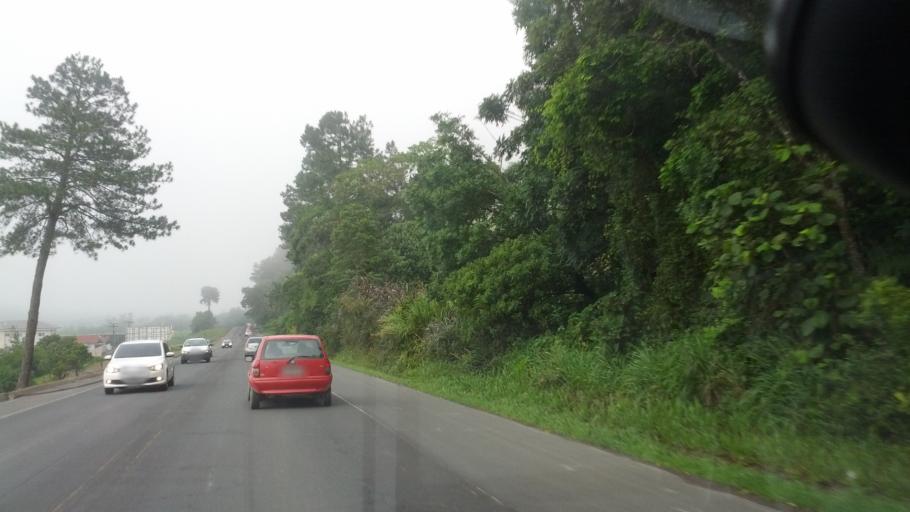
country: BR
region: Santa Catarina
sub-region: Rio Do Sul
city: Rio do Sul
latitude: -27.2671
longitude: -49.7285
